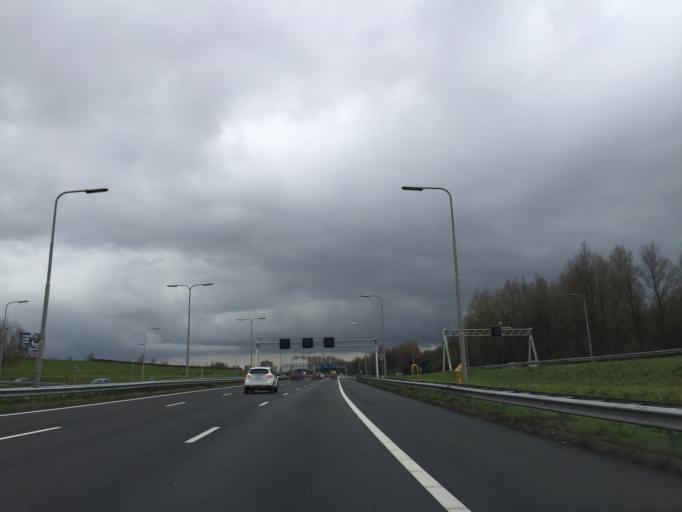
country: NL
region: South Holland
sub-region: Gemeente Den Haag
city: Ypenburg
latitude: 52.0382
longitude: 4.3518
